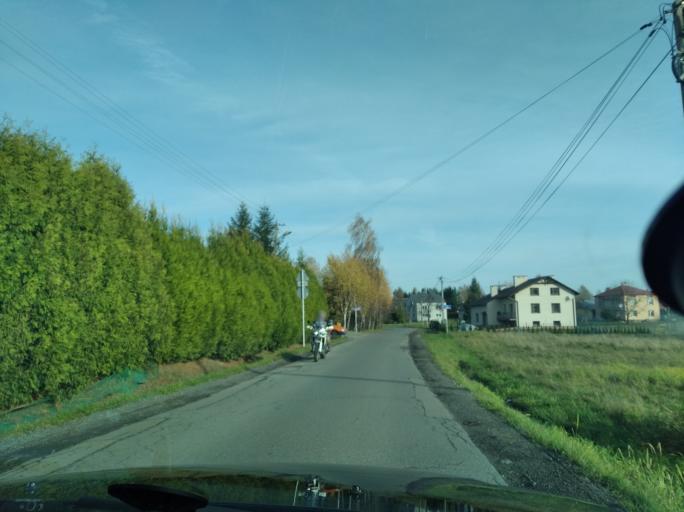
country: PL
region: Subcarpathian Voivodeship
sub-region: Powiat rzeszowski
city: Tyczyn
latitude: 50.0006
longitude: 22.0691
